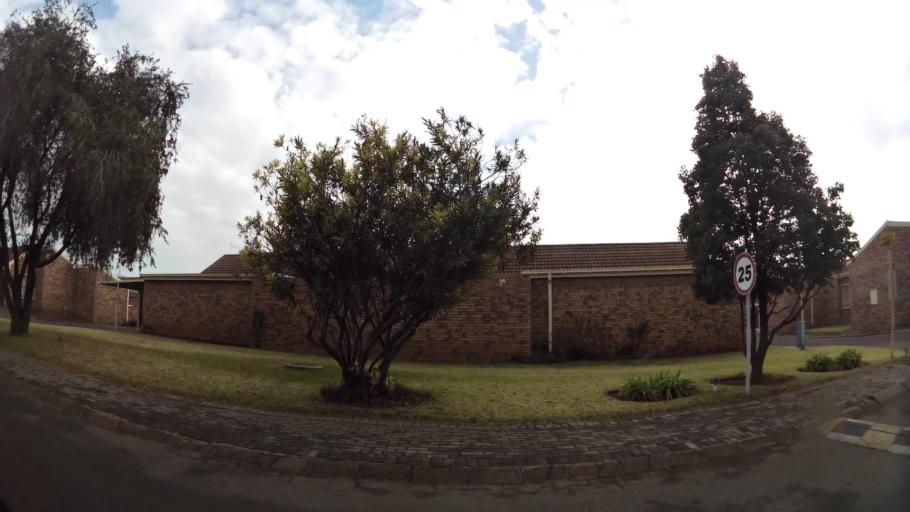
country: ZA
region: Gauteng
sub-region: Sedibeng District Municipality
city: Vanderbijlpark
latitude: -26.7058
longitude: 27.8285
